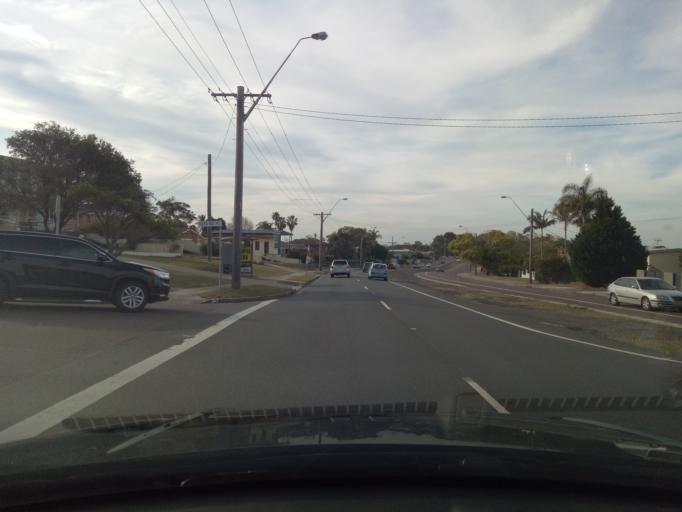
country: AU
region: New South Wales
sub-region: Wyong Shire
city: Bateau Bay
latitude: -33.3857
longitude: 151.4725
